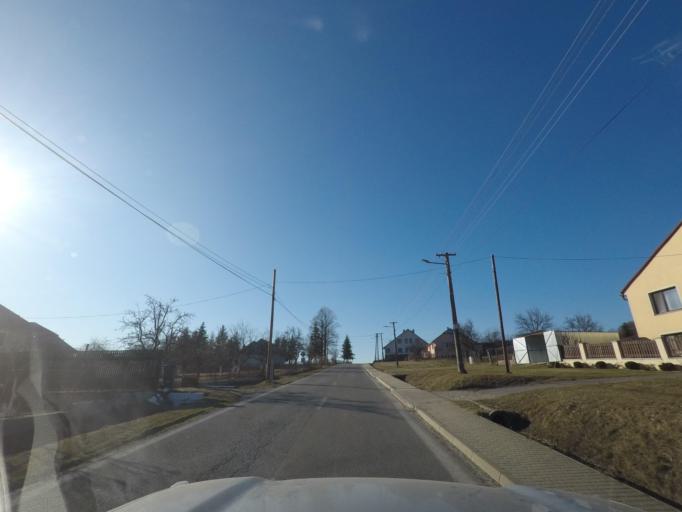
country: SK
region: Presovsky
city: Medzilaborce
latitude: 49.2226
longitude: 21.9741
